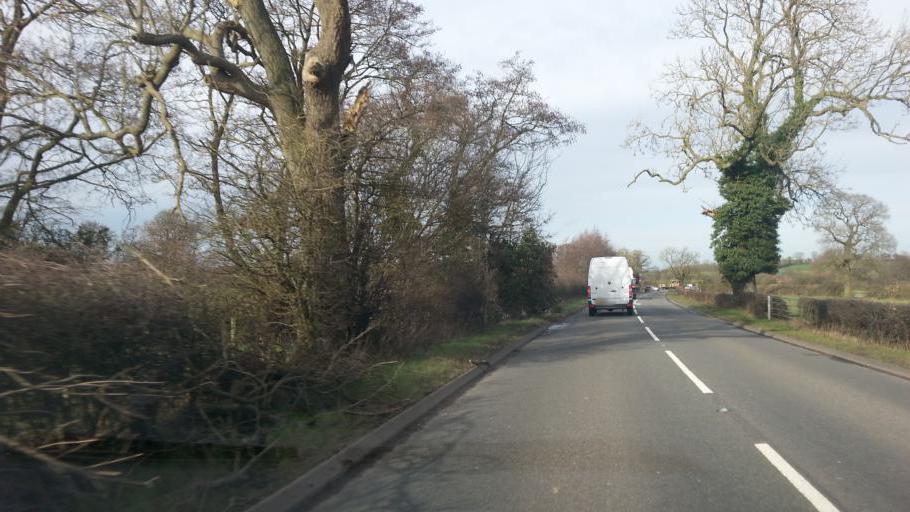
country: GB
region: England
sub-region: Staffordshire
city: Uttoxeter
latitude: 52.8745
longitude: -1.9390
